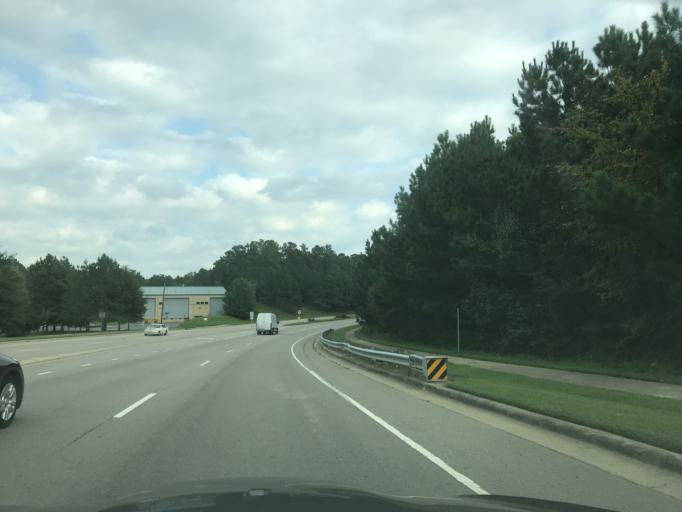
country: US
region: North Carolina
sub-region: Durham County
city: Durham
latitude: 35.9387
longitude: -78.9027
